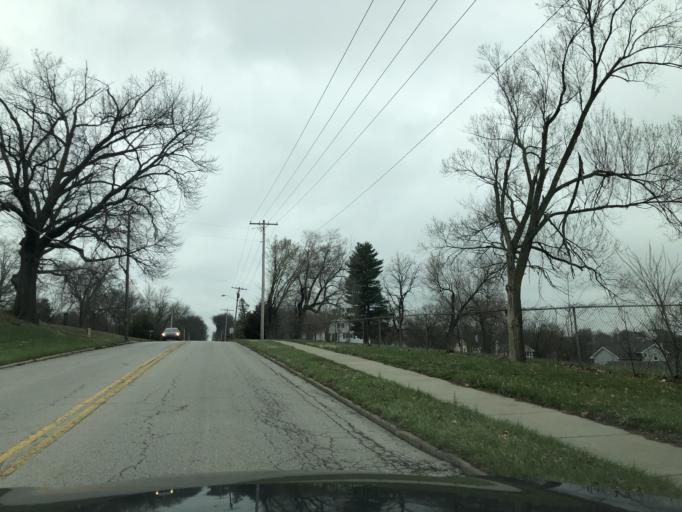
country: US
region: Kansas
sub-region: Leavenworth County
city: Leavenworth
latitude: 39.2812
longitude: -94.9185
